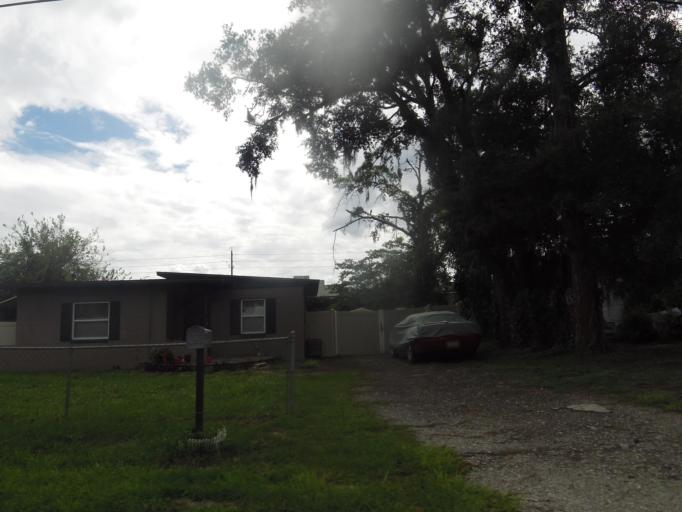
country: US
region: Florida
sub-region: Duval County
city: Jacksonville
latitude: 30.2725
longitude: -81.5579
